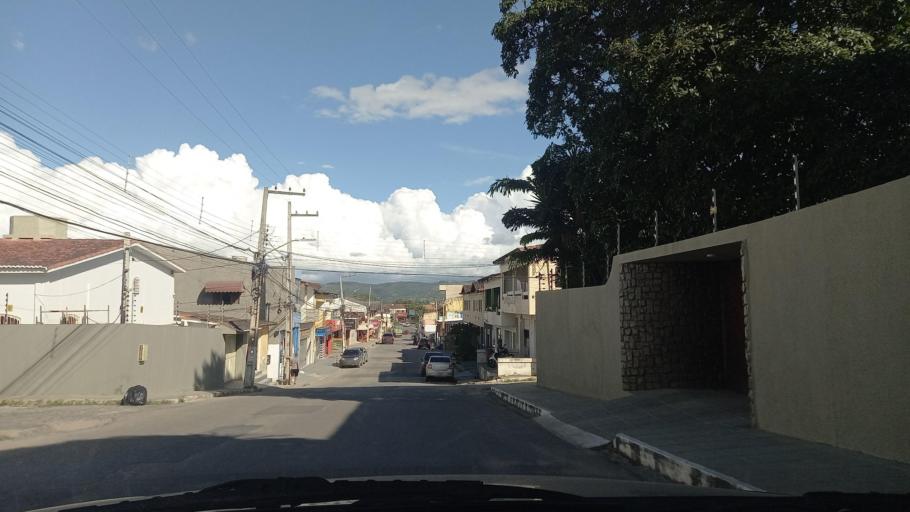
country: BR
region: Pernambuco
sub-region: Gravata
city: Gravata
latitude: -8.1966
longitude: -35.5638
